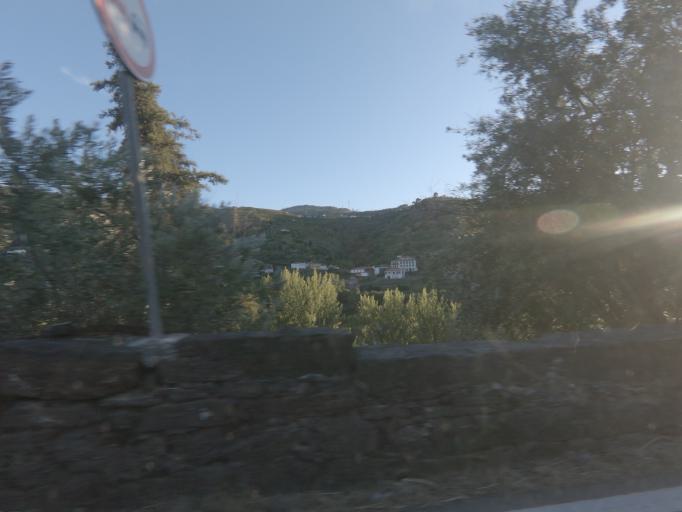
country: PT
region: Vila Real
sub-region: Mesao Frio
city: Mesao Frio
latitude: 41.1579
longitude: -7.8533
